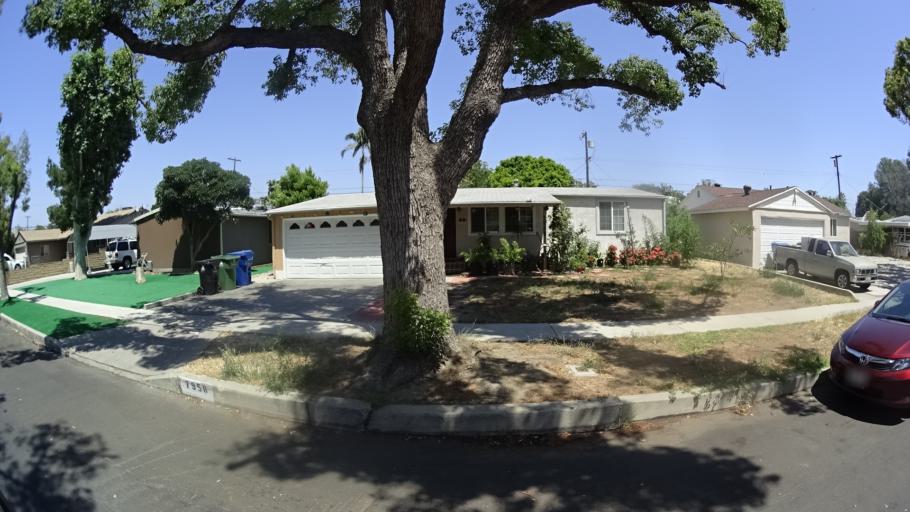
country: US
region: California
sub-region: Los Angeles County
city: Van Nuys
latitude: 34.2157
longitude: -118.4381
